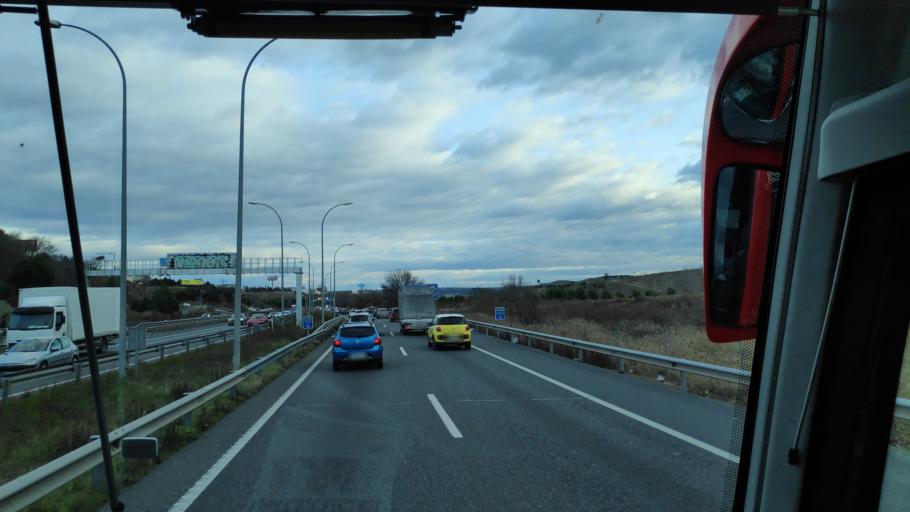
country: ES
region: Madrid
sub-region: Provincia de Madrid
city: Vaciamadrid
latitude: 40.3486
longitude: -3.5467
